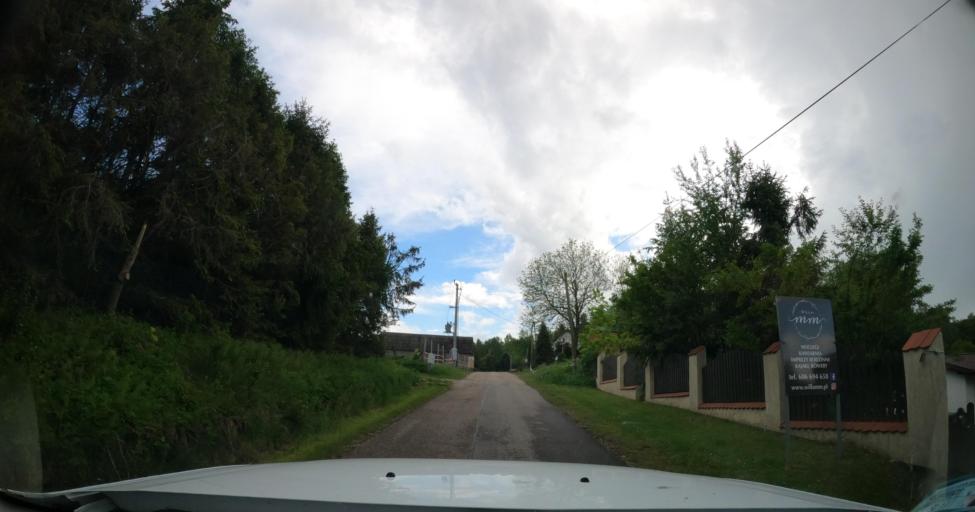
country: PL
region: Pomeranian Voivodeship
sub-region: Powiat kartuski
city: Garcz
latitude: 54.3337
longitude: 18.1391
